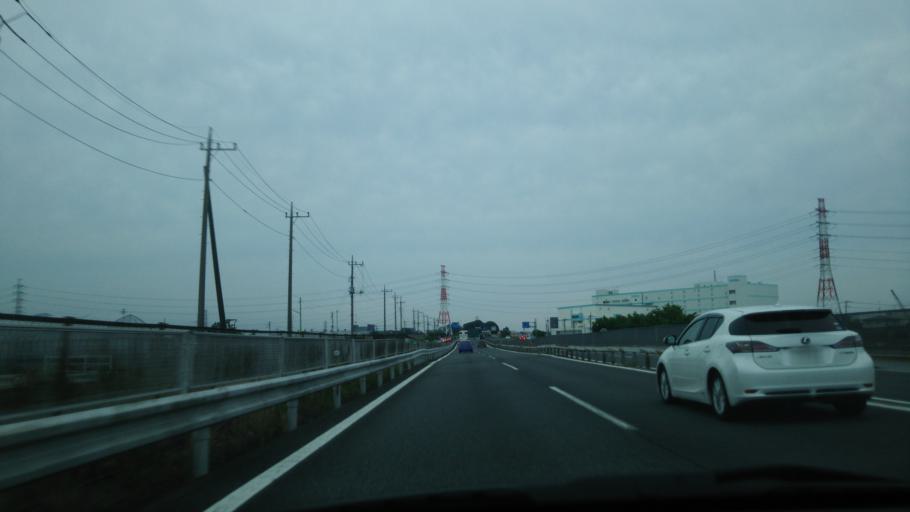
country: JP
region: Kanagawa
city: Isehara
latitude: 35.3989
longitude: 139.3349
